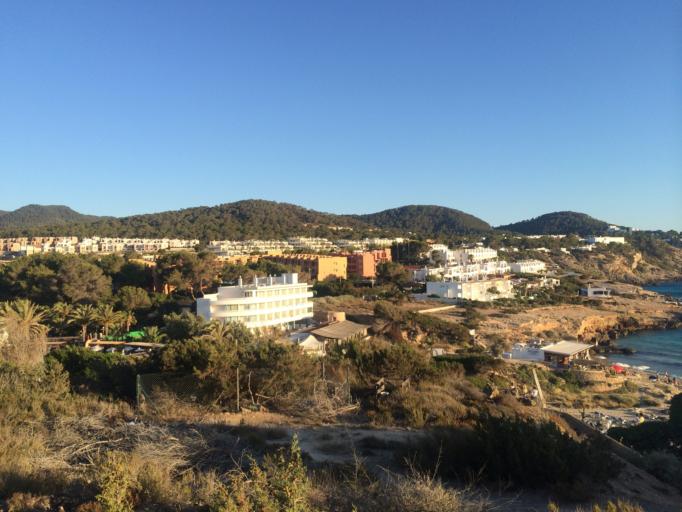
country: ES
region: Balearic Islands
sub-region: Illes Balears
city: Sant Josep de sa Talaia
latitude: 38.9404
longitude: 1.2371
